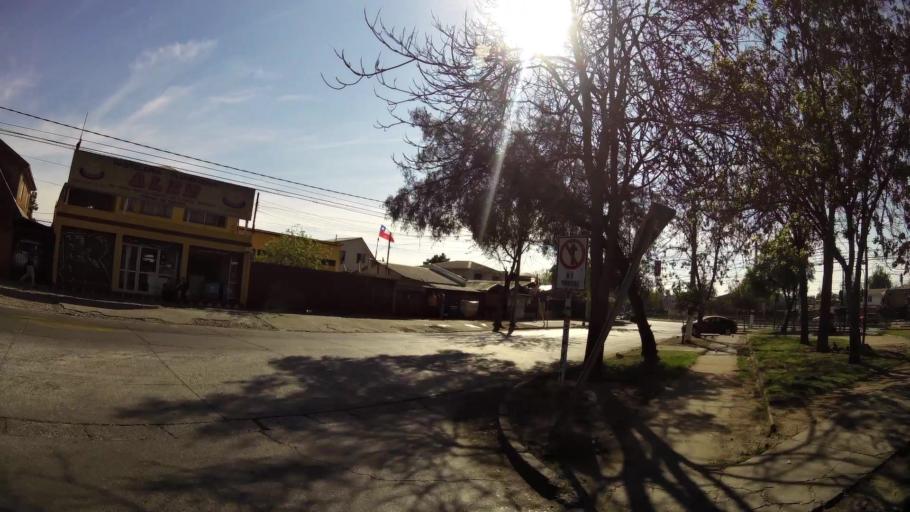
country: CL
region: Santiago Metropolitan
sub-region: Provincia de Santiago
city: Villa Presidente Frei, Nunoa, Santiago, Chile
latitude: -33.4712
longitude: -70.5688
